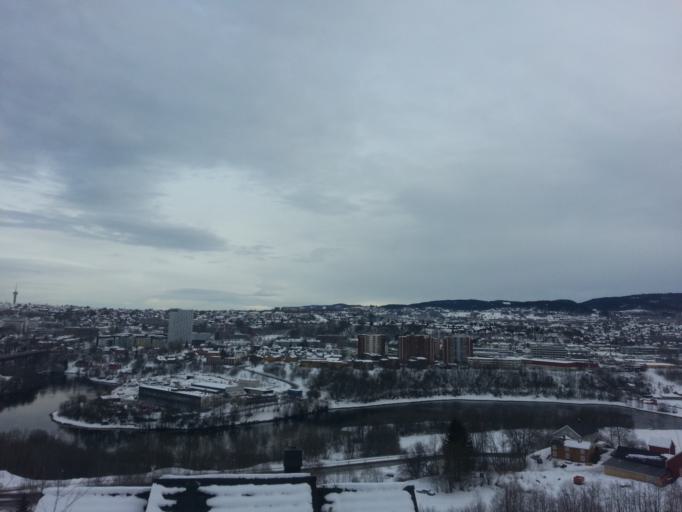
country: NO
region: Sor-Trondelag
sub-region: Trondheim
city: Trondheim
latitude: 63.4086
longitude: 10.3804
